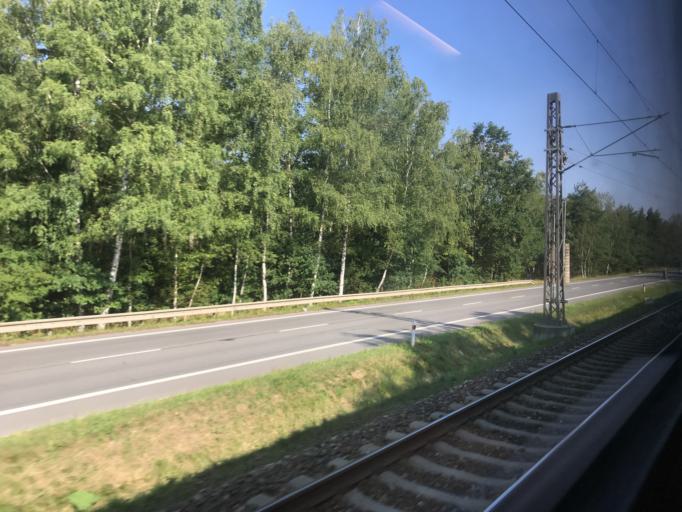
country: CZ
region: Jihocesky
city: Plana nad Luznici
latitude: 49.3374
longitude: 14.7127
